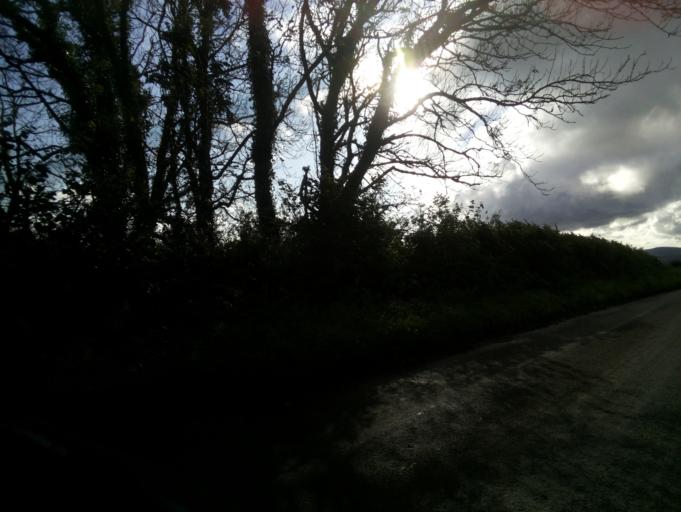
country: GB
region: England
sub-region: Devon
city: Totnes
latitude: 50.3723
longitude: -3.7461
